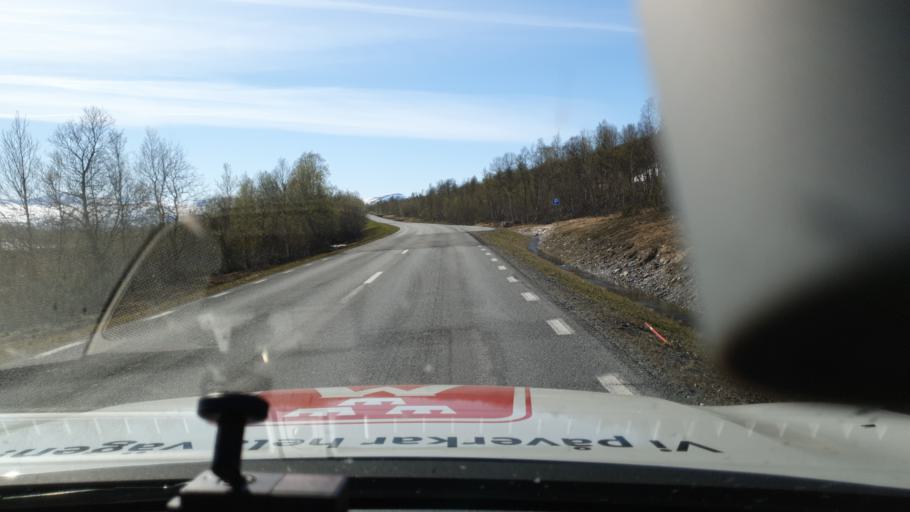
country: NO
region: Nordland
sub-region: Rana
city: Mo i Rana
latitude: 66.0397
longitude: 15.0199
